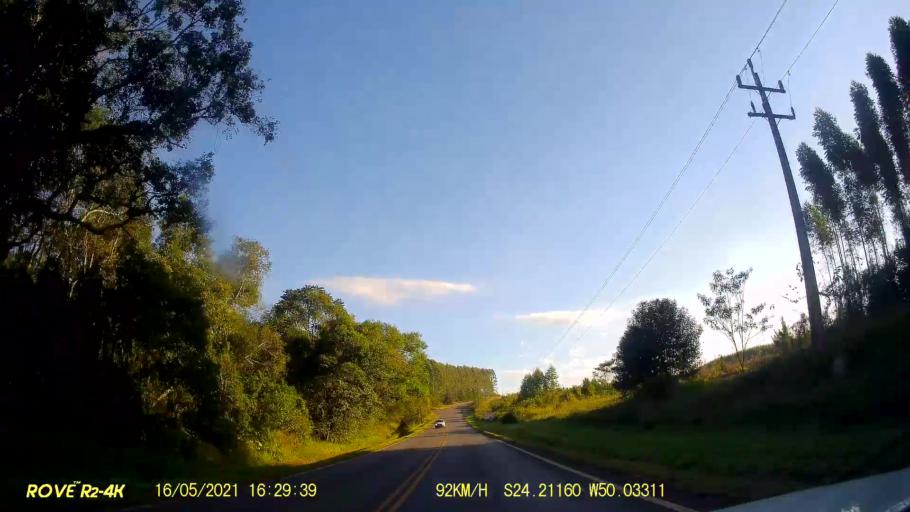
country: BR
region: Parana
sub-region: Jaguariaiva
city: Jaguariaiva
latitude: -24.2116
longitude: -50.0333
